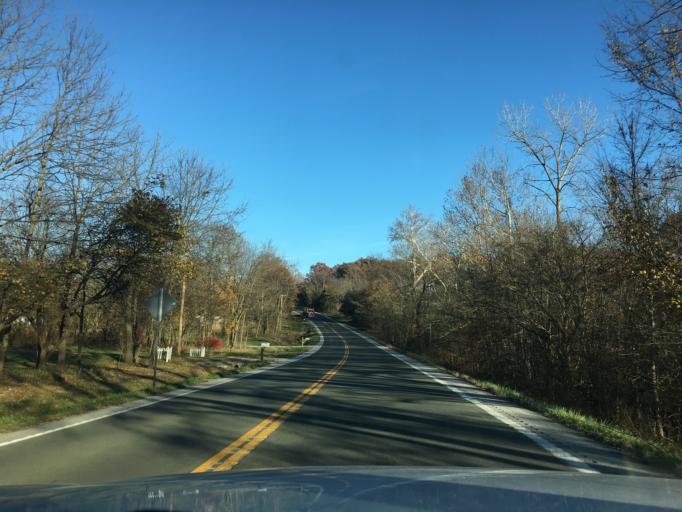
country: US
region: Missouri
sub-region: Franklin County
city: New Haven
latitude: 38.5982
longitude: -91.2502
